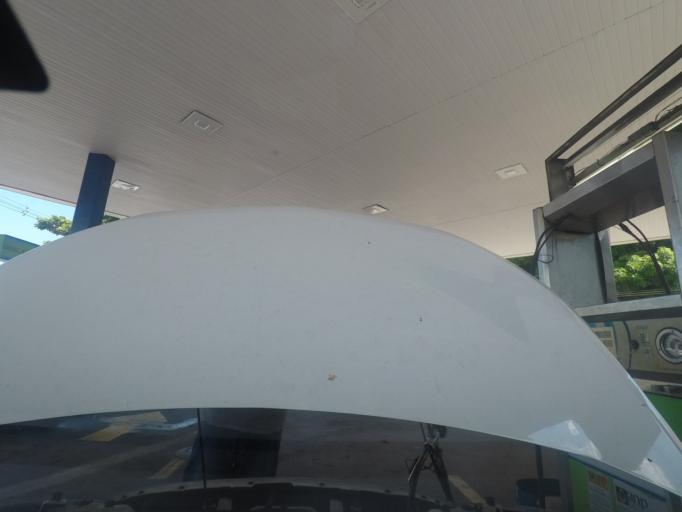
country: BR
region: Rio de Janeiro
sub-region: Rio De Janeiro
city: Rio de Janeiro
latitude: -22.8883
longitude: -43.2238
